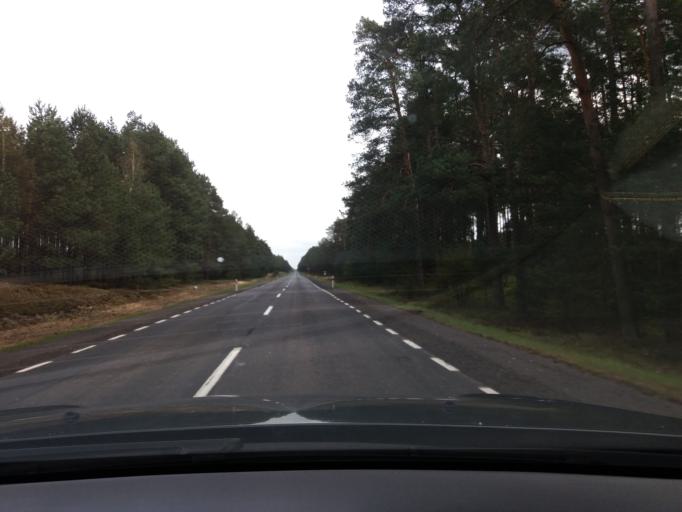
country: PL
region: Lubusz
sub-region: Powiat sulecinski
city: Lubniewice
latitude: 52.5892
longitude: 15.2816
